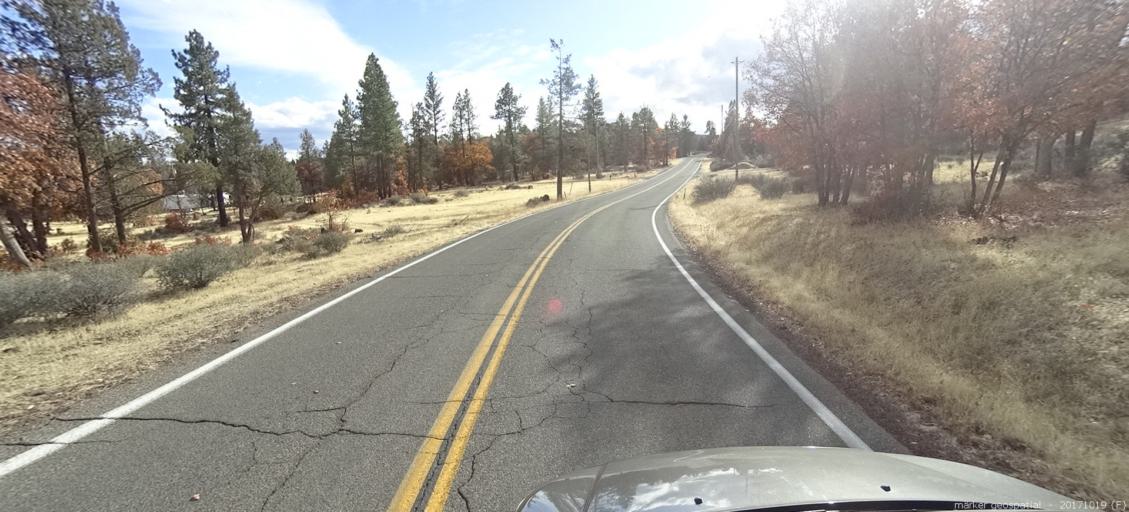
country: US
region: California
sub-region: Shasta County
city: Burney
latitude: 40.9696
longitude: -121.4331
